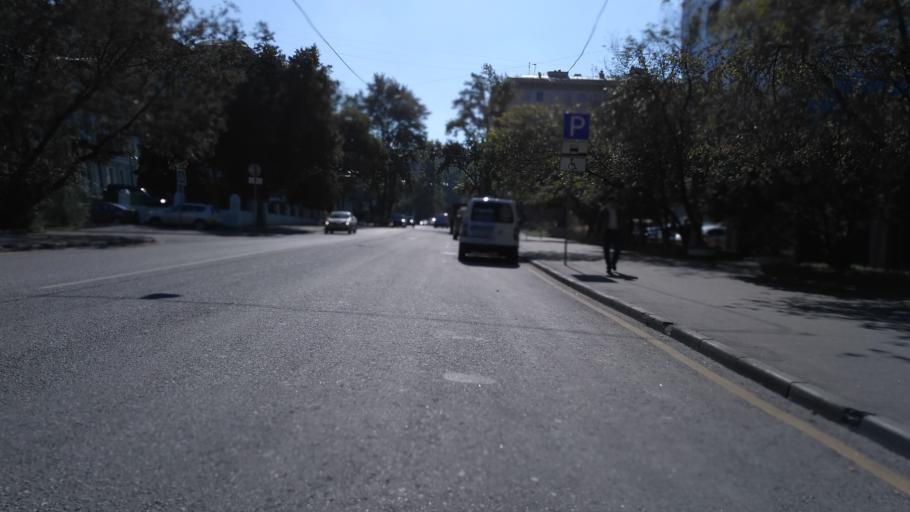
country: RU
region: Moscow
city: Sokol'niki
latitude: 55.7856
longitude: 37.6596
